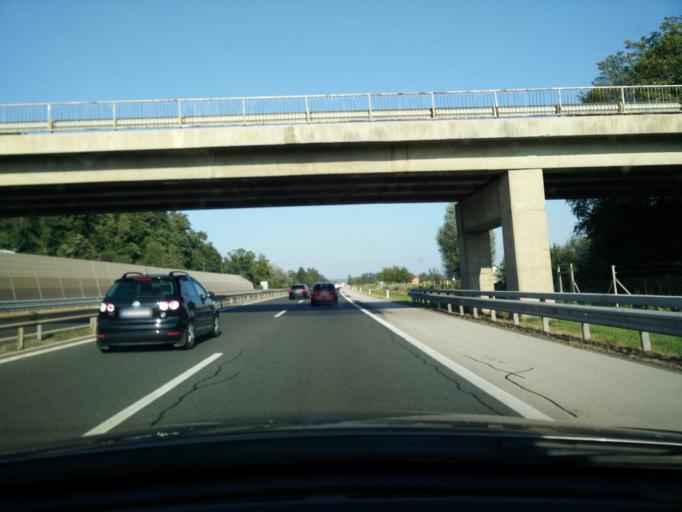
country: SI
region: Log-Dragomer
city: Dragomer
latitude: 46.0179
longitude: 14.3919
